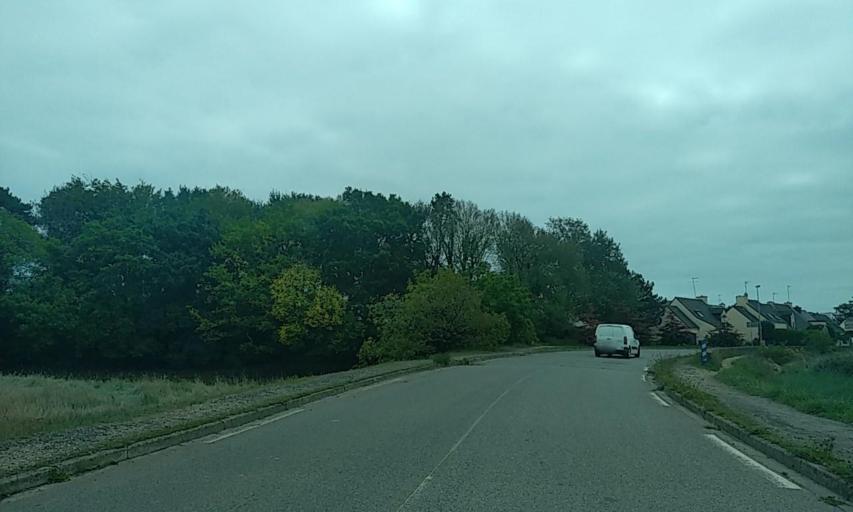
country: FR
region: Brittany
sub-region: Departement du Morbihan
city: Lorient
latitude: 47.7706
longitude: -3.3607
